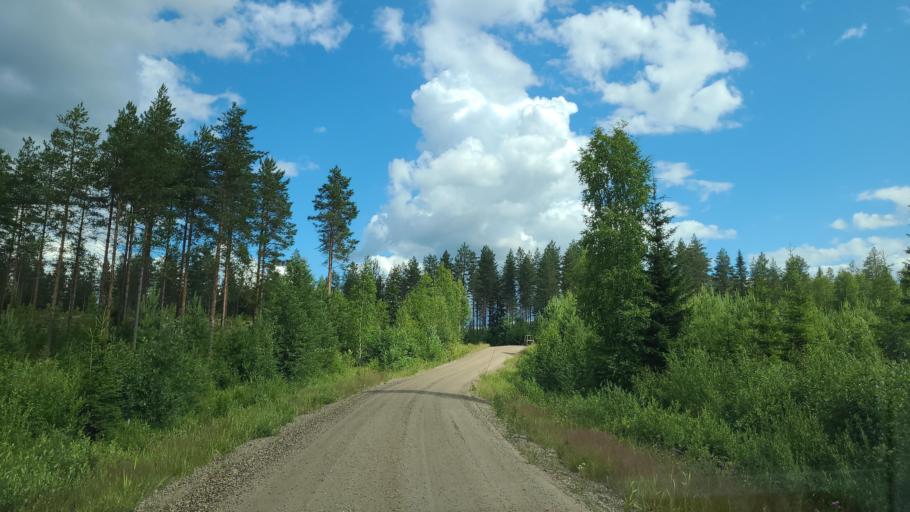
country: FI
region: Northern Savo
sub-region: Koillis-Savo
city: Kaavi
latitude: 63.0293
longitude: 28.7844
